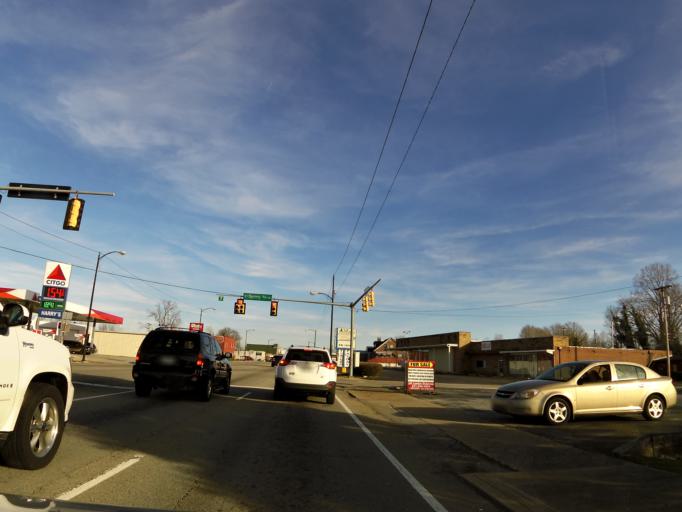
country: US
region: Tennessee
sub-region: White County
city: Sparta
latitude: 35.9315
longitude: -85.4756
